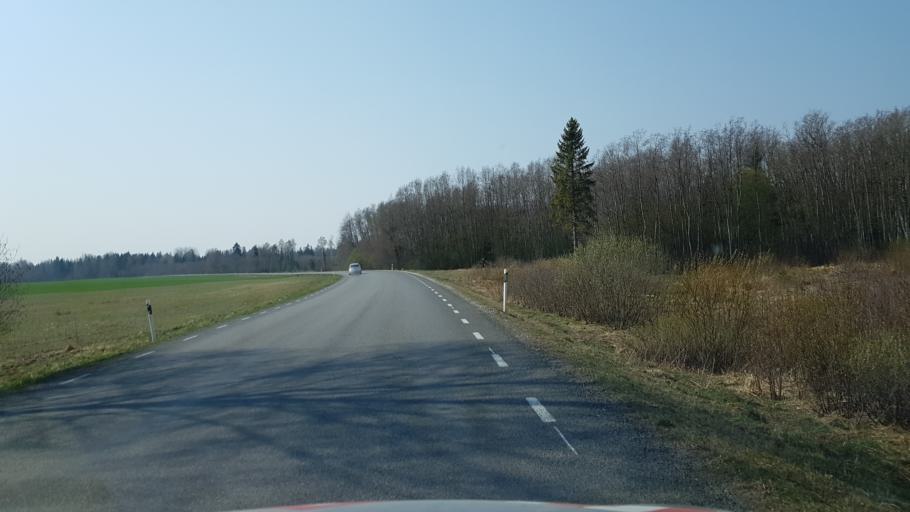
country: EE
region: Raplamaa
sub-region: Kehtna vald
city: Kehtna
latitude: 59.0371
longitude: 24.9292
